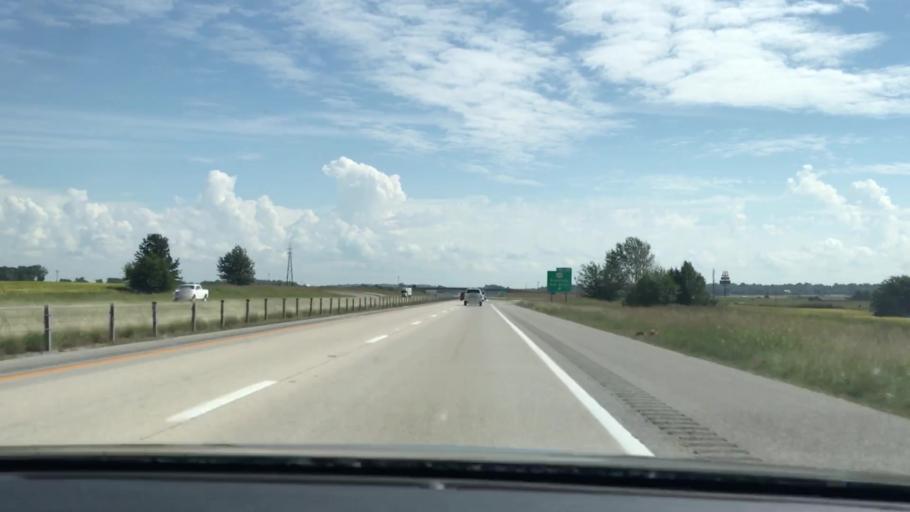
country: US
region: Kentucky
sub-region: Christian County
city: Oak Grove
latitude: 36.6849
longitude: -87.4113
